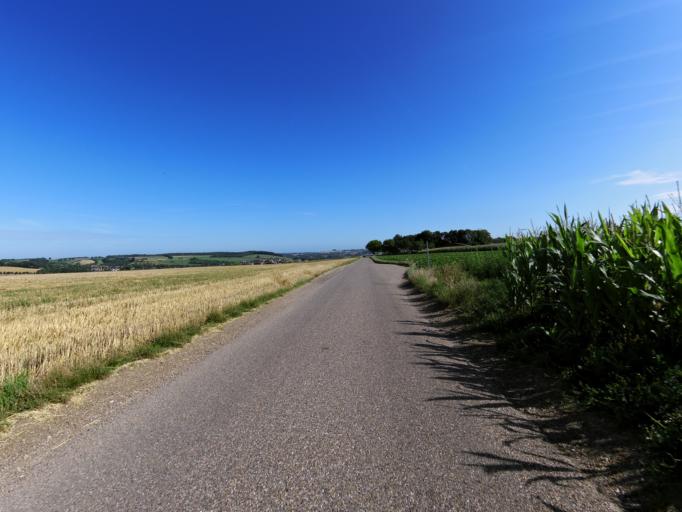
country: NL
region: Limburg
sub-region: Valkenburg aan de Geul
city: Schin op Geul
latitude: 50.8026
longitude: 5.8910
